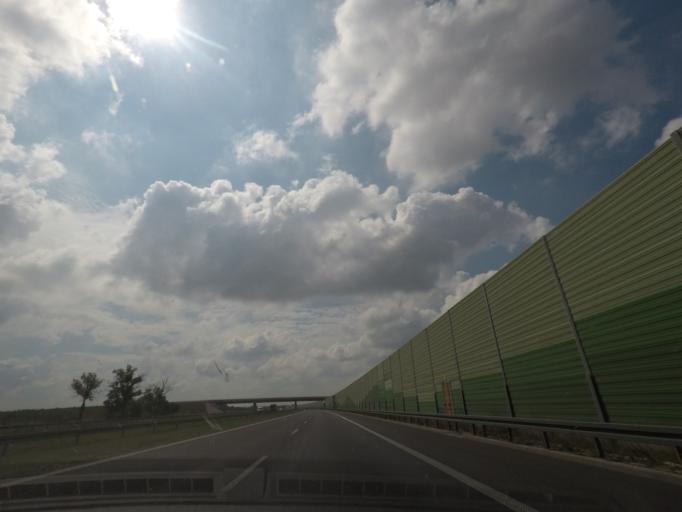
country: PL
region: Lodz Voivodeship
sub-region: Powiat kutnowski
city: Krzyzanow
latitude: 52.1502
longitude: 19.4815
